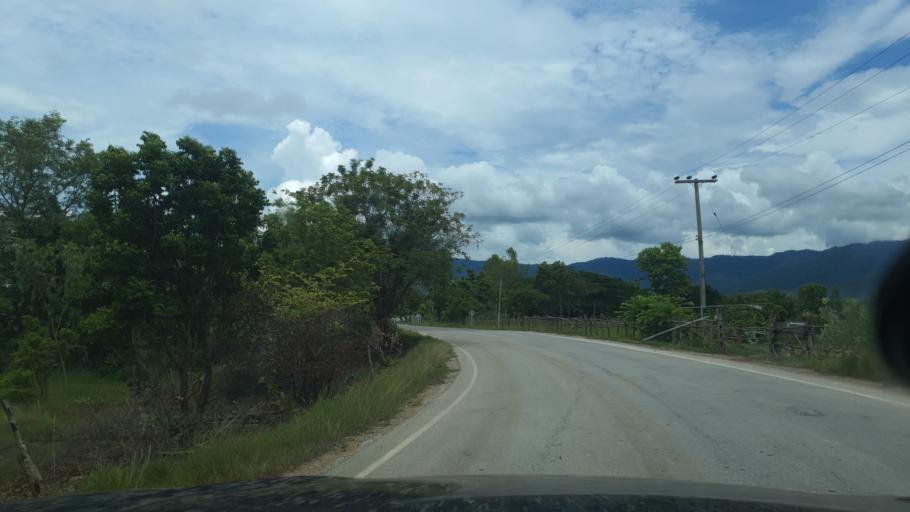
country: TH
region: Lampang
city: Sop Prap
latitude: 17.9139
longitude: 99.3921
